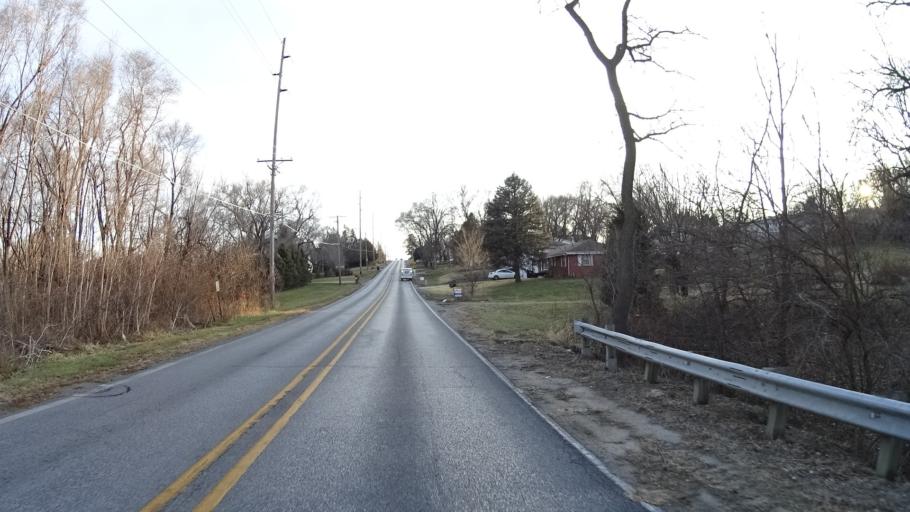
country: US
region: Nebraska
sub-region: Sarpy County
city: La Vista
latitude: 41.1750
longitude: -95.9673
